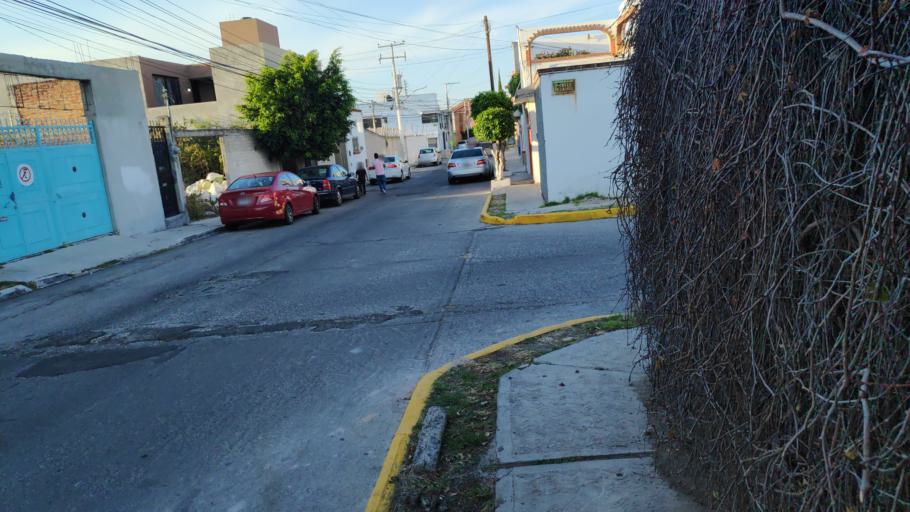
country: MX
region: Queretaro
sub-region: Queretaro
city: Santiago de Queretaro
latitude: 20.5812
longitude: -100.3822
